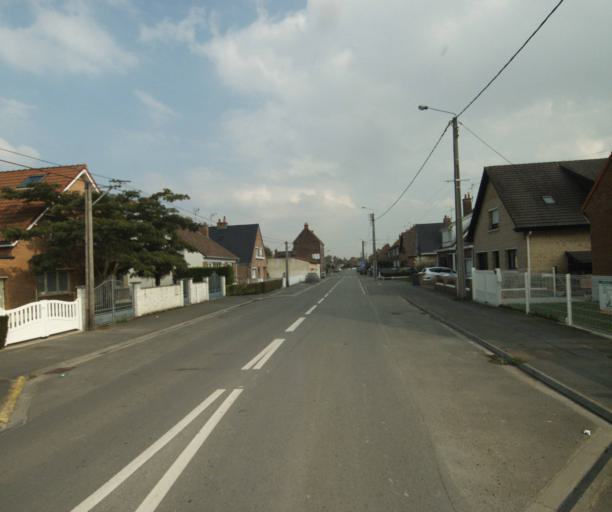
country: FR
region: Nord-Pas-de-Calais
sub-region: Departement du Nord
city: Emmerin
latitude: 50.5782
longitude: 2.9832
